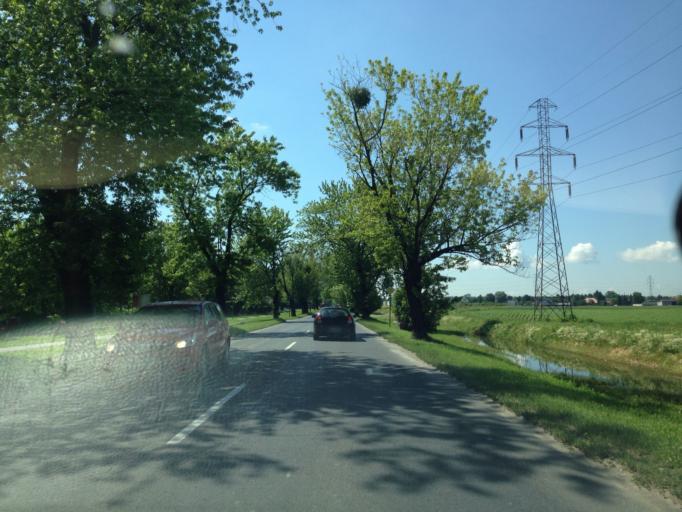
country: PL
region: Masovian Voivodeship
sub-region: Warszawa
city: Bemowo
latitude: 52.2308
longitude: 20.8969
